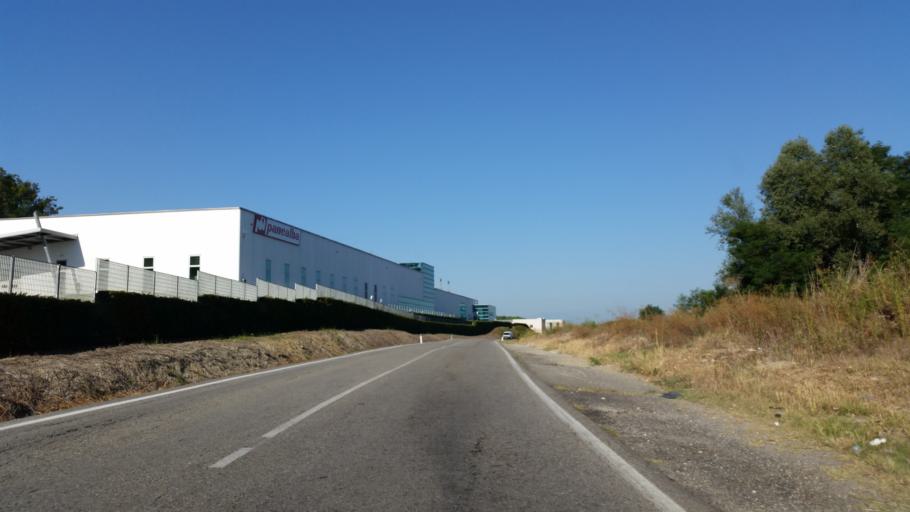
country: IT
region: Piedmont
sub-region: Provincia di Cuneo
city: Verduno
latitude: 44.6796
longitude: 7.9275
